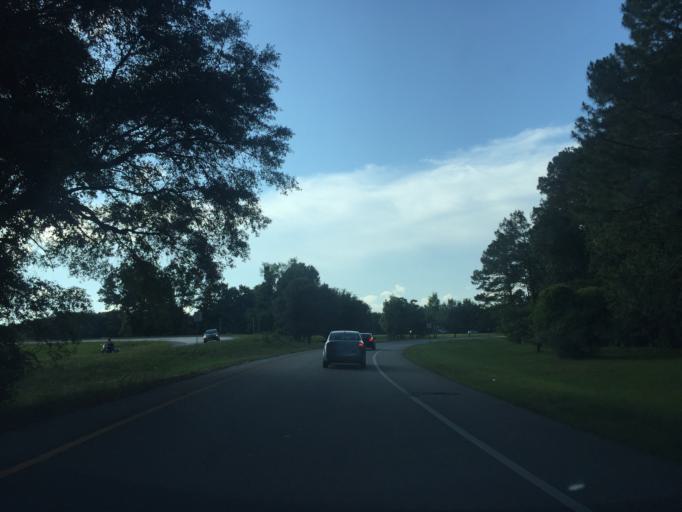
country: US
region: Georgia
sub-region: Chatham County
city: Pooler
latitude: 32.0747
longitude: -81.2434
